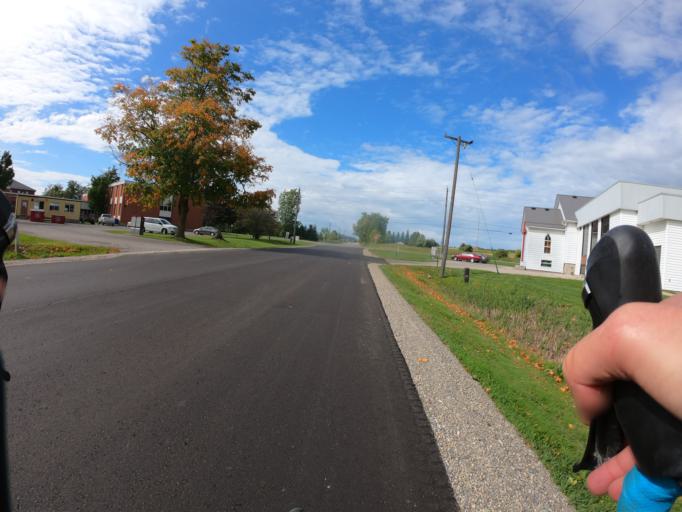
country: CA
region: Ontario
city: Kitchener
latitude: 43.3852
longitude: -80.6269
